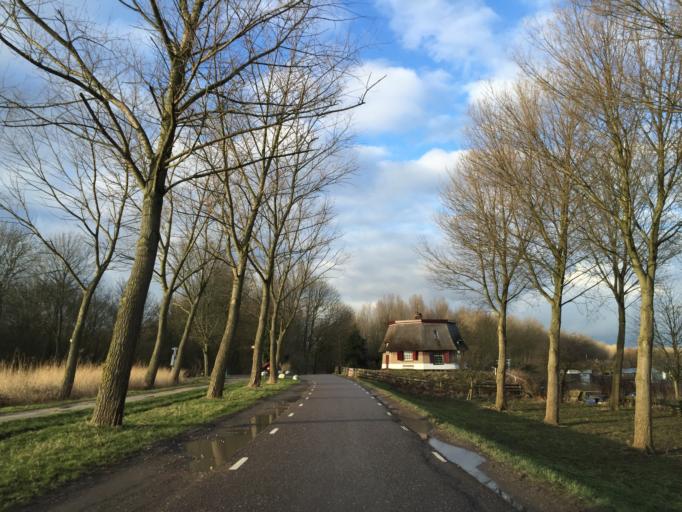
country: NL
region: South Holland
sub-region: Gemeente Den Haag
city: Ypenburg
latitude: 52.0208
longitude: 4.3885
